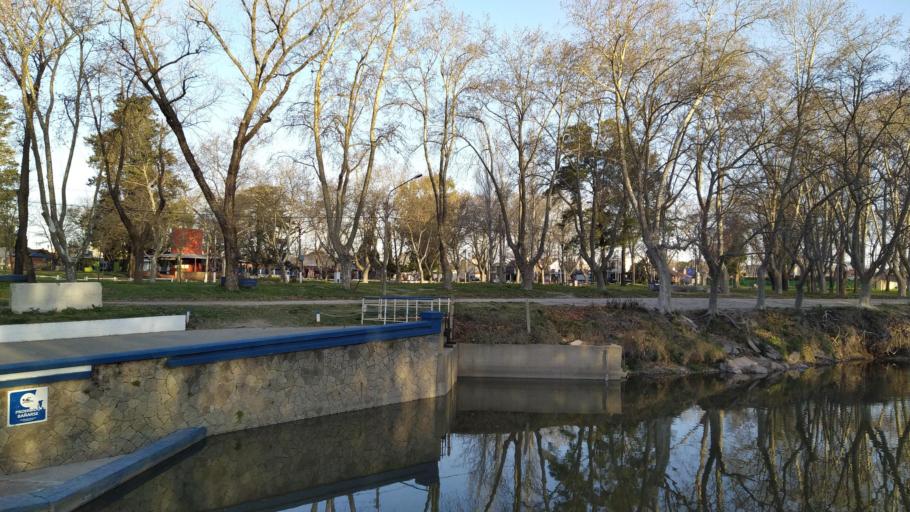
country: AR
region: Buenos Aires
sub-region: Partido de Salto
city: Salto
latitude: -34.2844
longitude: -60.2572
